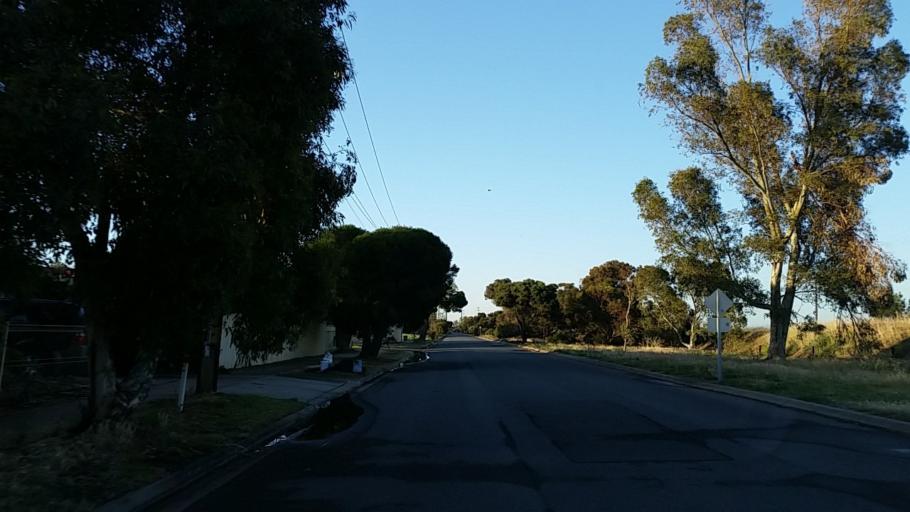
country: AU
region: South Australia
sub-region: Port Adelaide Enfield
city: Birkenhead
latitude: -34.8110
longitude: 138.5071
